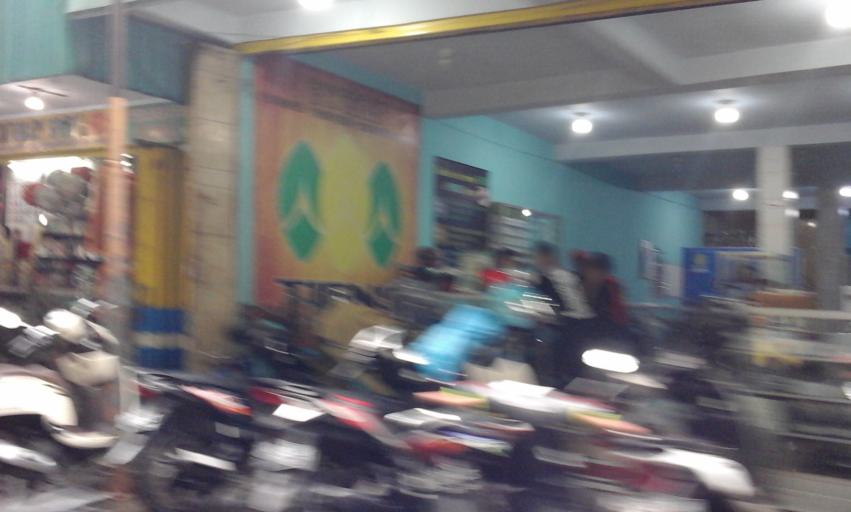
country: ID
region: East Java
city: Lumajang
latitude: -8.1328
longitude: 113.2208
